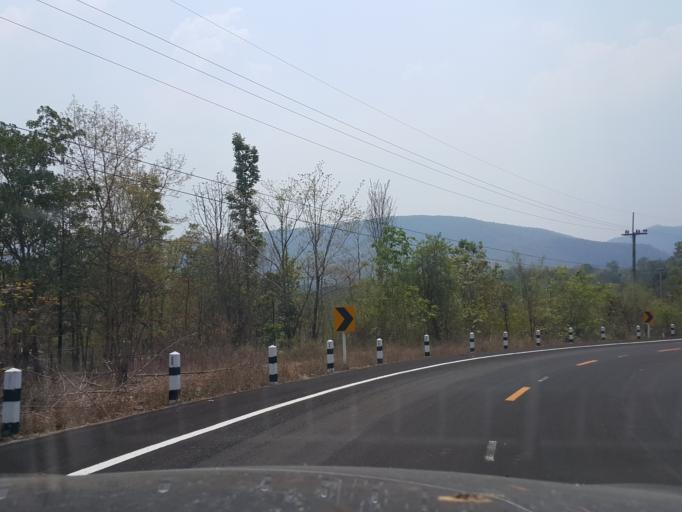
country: TH
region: Lampang
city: Mae Phrik
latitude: 17.4890
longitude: 99.0903
